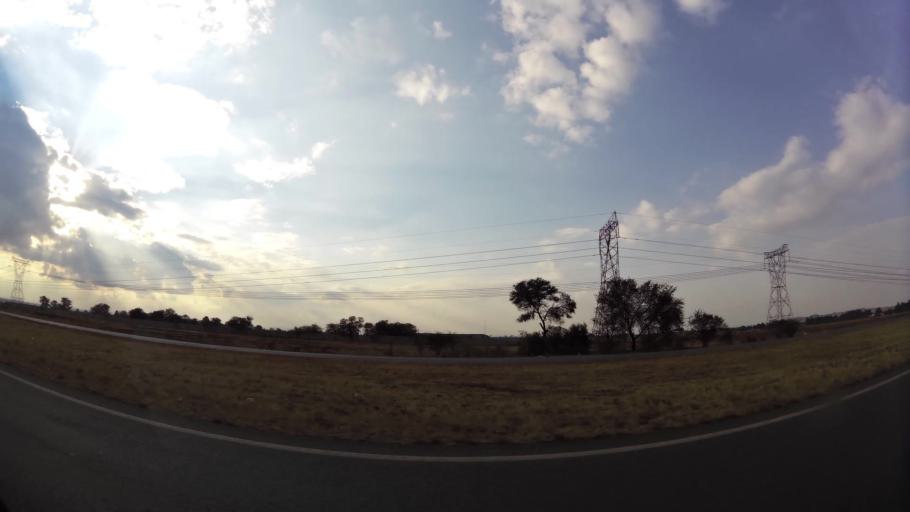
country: ZA
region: Gauteng
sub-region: Sedibeng District Municipality
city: Vanderbijlpark
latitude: -26.6185
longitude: 27.8392
